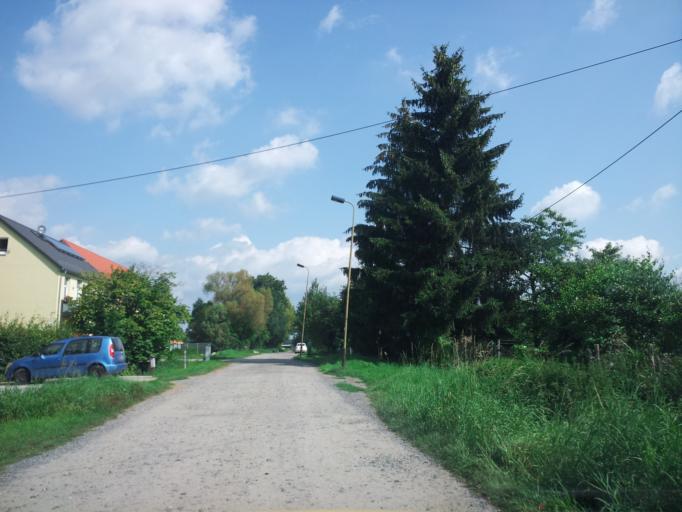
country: DE
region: Brandenburg
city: Treuenbrietzen
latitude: 52.0974
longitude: 12.8656
